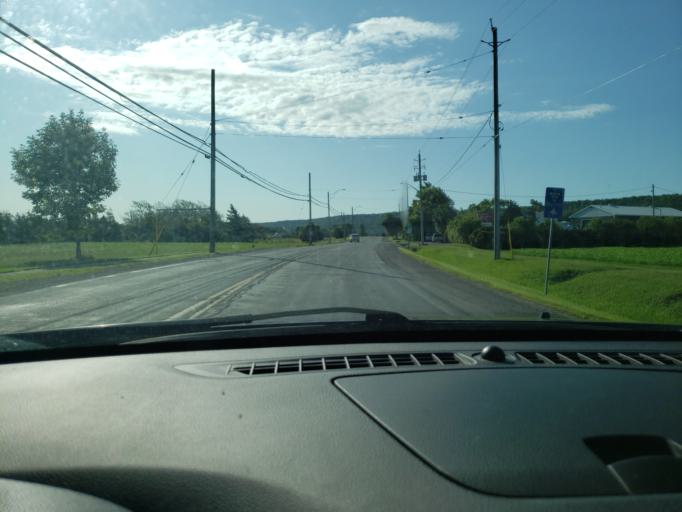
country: CA
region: Ontario
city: Hamilton
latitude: 43.2039
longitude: -79.6151
